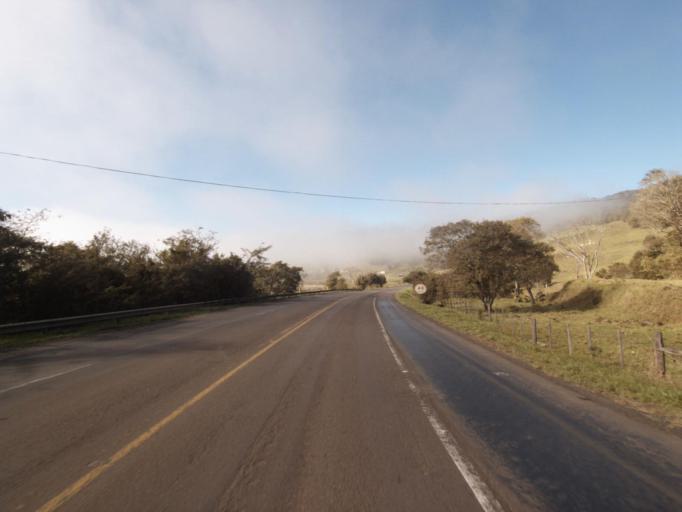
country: BR
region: Rio Grande do Sul
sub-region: Frederico Westphalen
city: Frederico Westphalen
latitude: -26.8226
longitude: -53.4231
